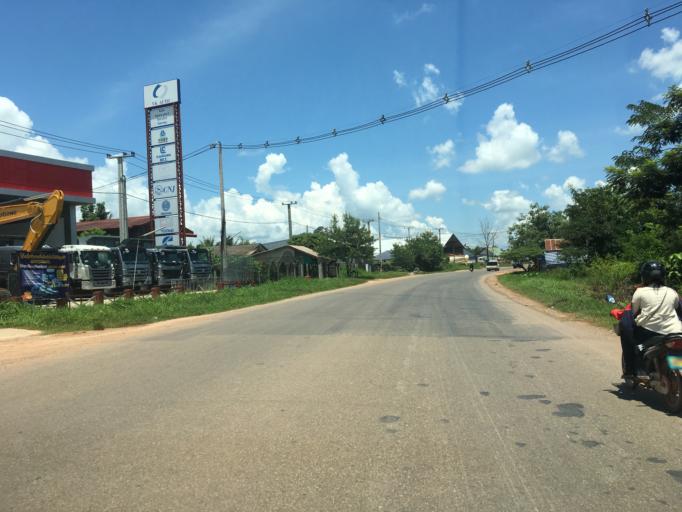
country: LA
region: Vientiane
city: Vientiane
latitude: 18.0950
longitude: 102.5102
